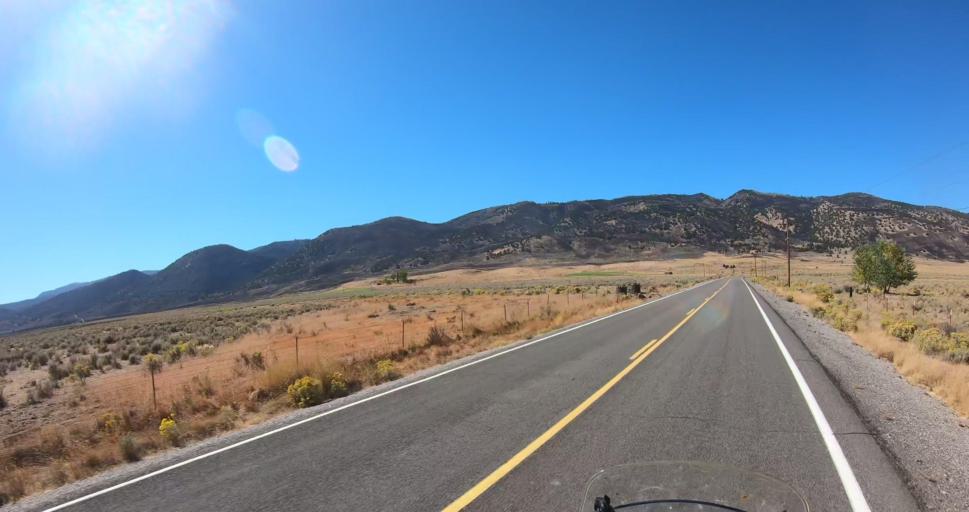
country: US
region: Oregon
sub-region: Lake County
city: Lakeview
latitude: 42.6195
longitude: -120.5024
